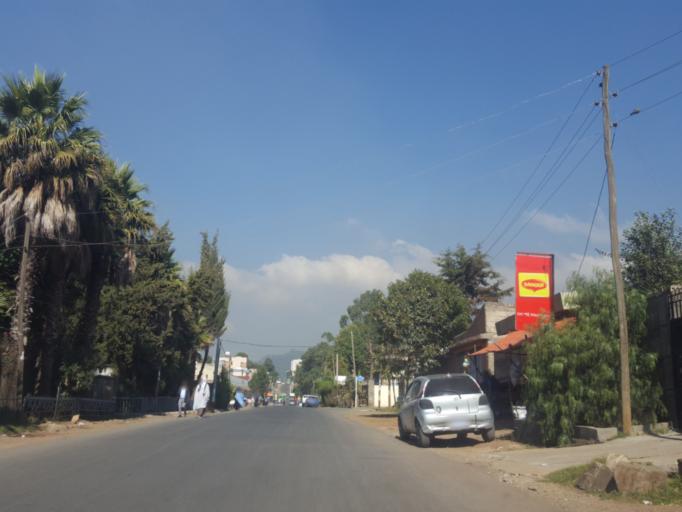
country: ET
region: Adis Abeba
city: Addis Ababa
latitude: 9.0537
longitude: 38.7305
